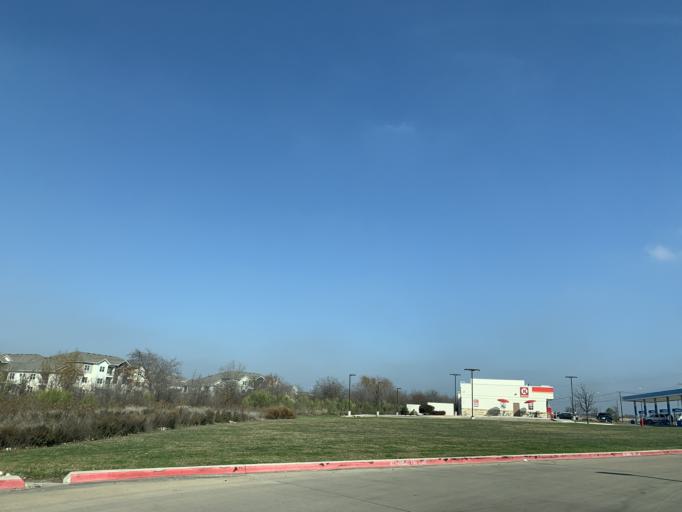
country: US
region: Texas
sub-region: Williamson County
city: Round Rock
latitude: 30.5436
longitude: -97.6510
